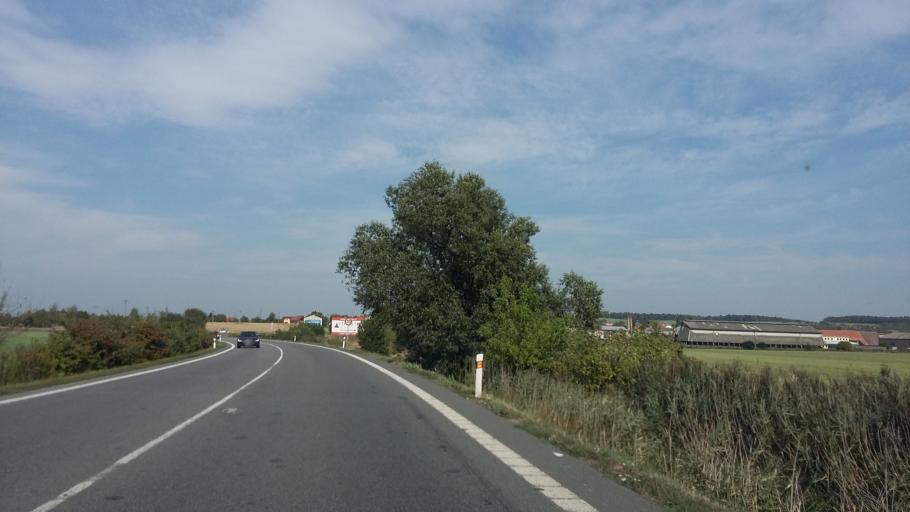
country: CZ
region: Central Bohemia
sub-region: Okres Kolin
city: Kolin
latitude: 50.0560
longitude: 15.2273
